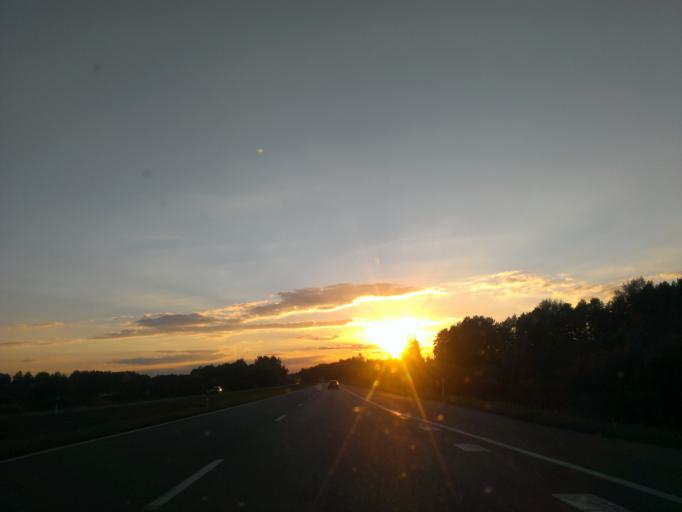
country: LV
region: Incukalns
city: Incukalns
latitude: 57.1285
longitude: 24.7131
